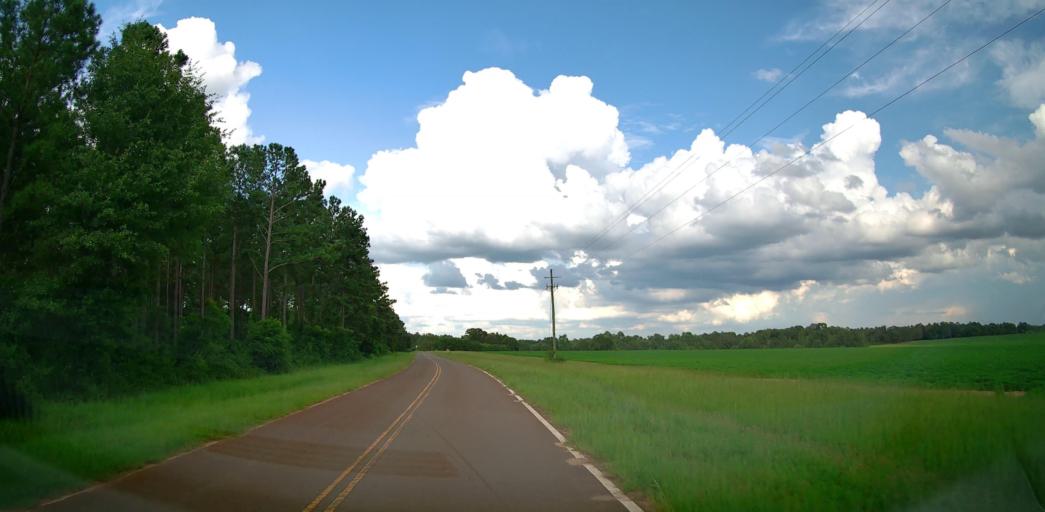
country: US
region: Georgia
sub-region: Bleckley County
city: Cochran
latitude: 32.4134
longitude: -83.4445
